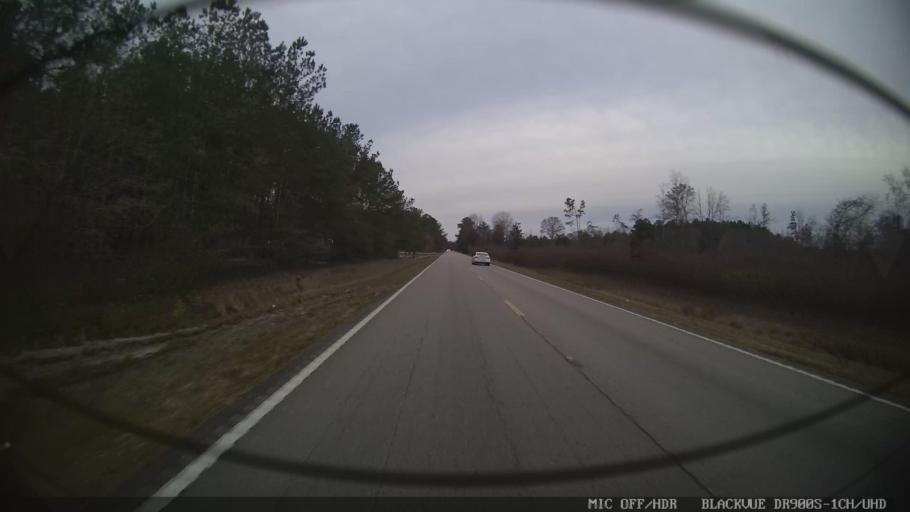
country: US
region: Mississippi
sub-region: Clarke County
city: Stonewall
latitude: 32.0339
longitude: -88.8719
